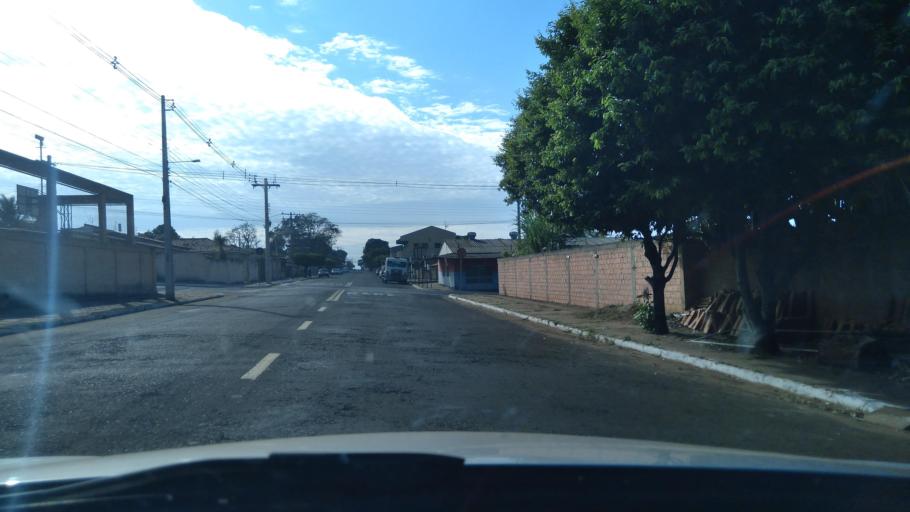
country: BR
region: Goias
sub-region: Mineiros
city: Mineiros
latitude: -17.5583
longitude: -52.5543
